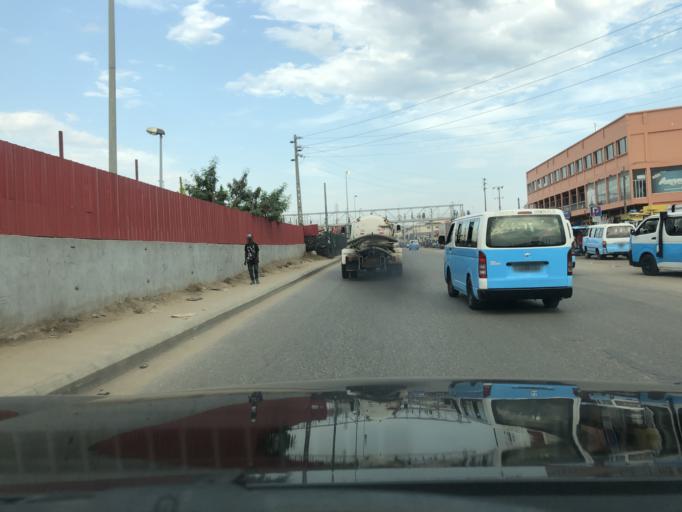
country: AO
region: Luanda
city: Luanda
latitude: -8.8811
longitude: 13.2536
